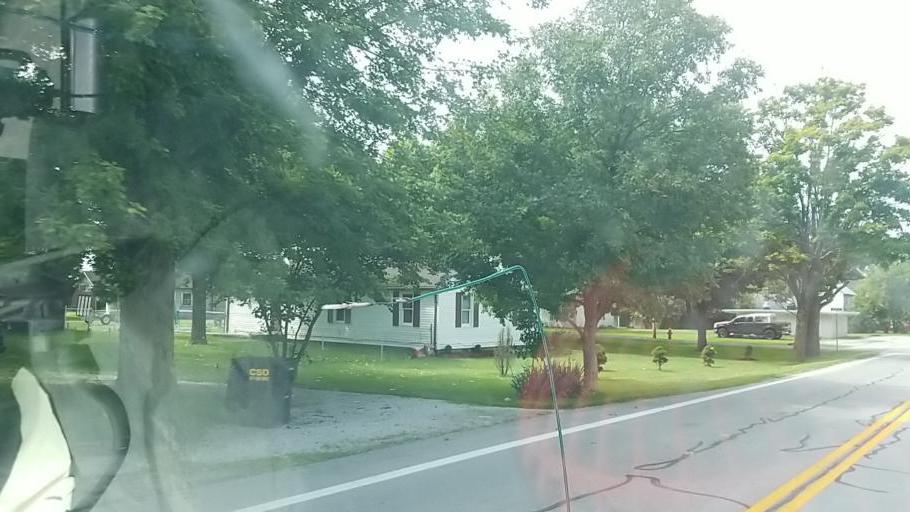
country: US
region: Ohio
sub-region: Fayette County
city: Jeffersonville
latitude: 39.6513
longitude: -83.5543
